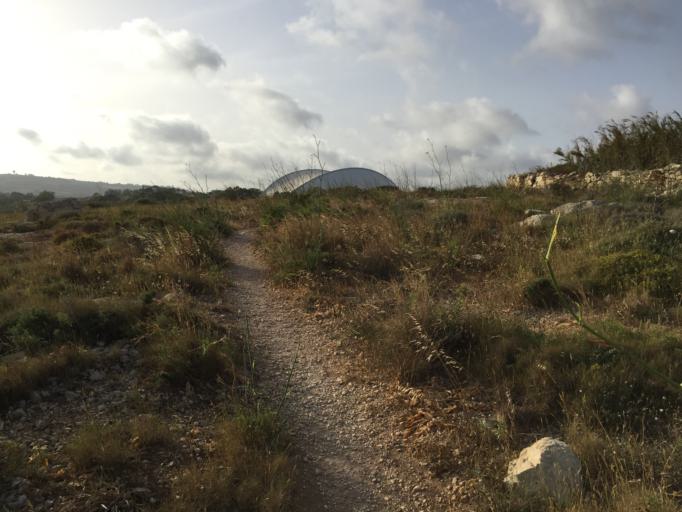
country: MT
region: Il-Qrendi
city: Qrendi
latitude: 35.8264
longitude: 14.4429
